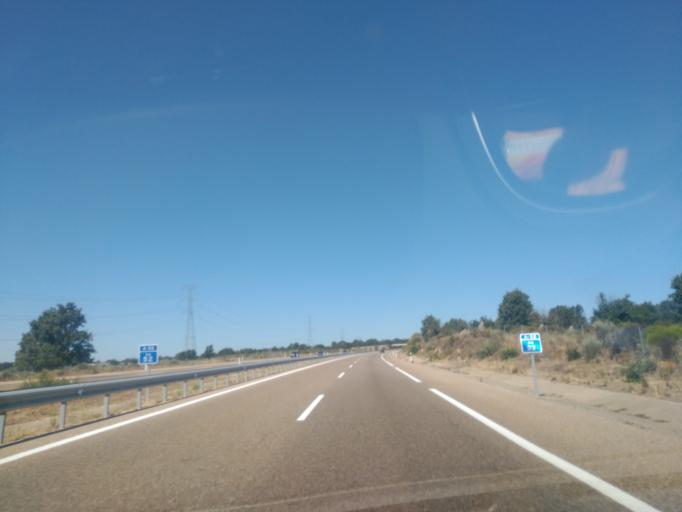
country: ES
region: Castille and Leon
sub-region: Provincia de Zamora
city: Mombuey
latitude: 42.0091
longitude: -6.2822
